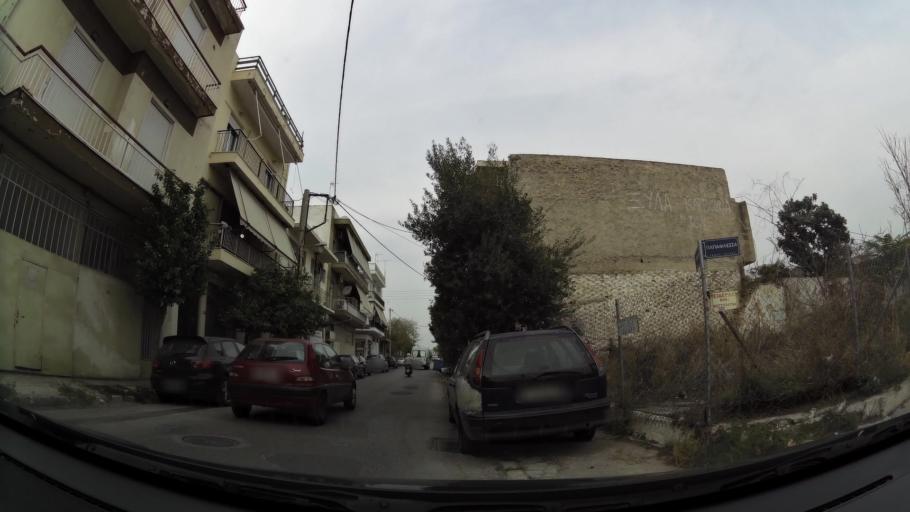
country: GR
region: Attica
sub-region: Nomarchia Athinas
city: Tavros
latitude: 37.9730
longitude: 23.6966
